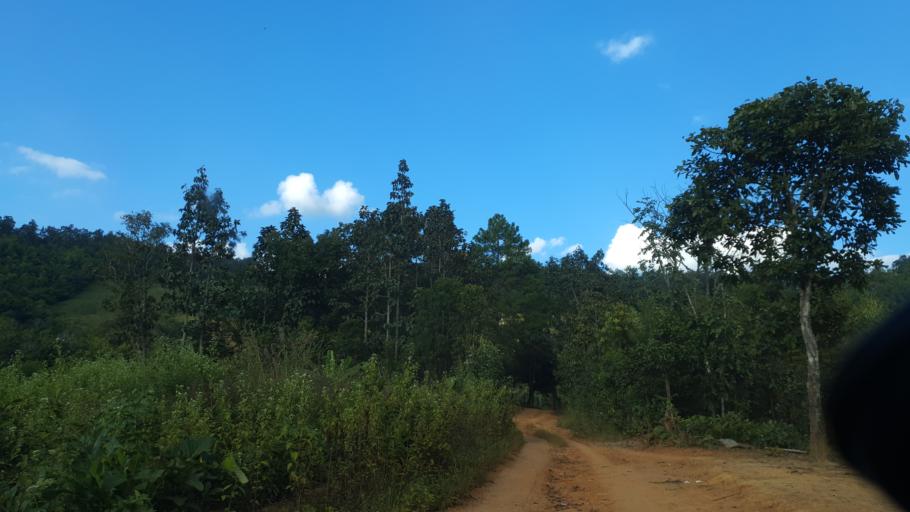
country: TH
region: Chiang Mai
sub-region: Amphoe Chiang Dao
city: Chiang Dao
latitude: 19.4038
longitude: 98.8304
